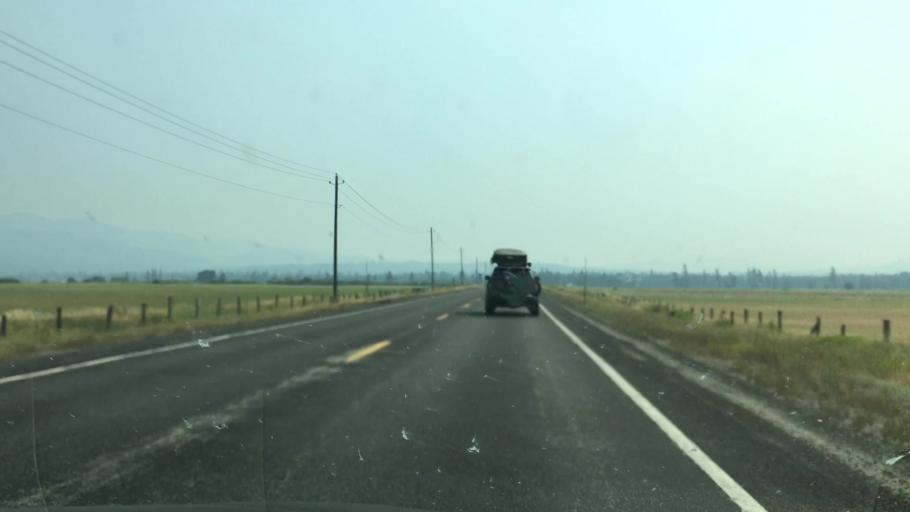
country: US
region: Idaho
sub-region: Valley County
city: Cascade
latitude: 44.4240
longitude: -115.9997
